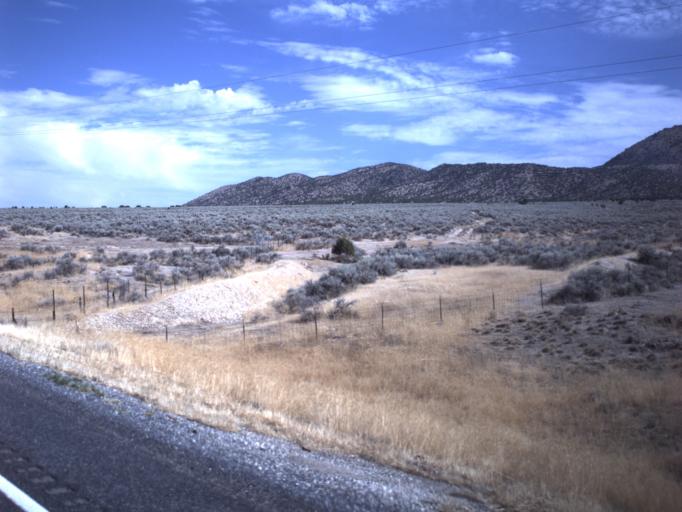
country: US
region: Utah
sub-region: Sanpete County
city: Gunnison
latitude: 39.2741
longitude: -111.8747
